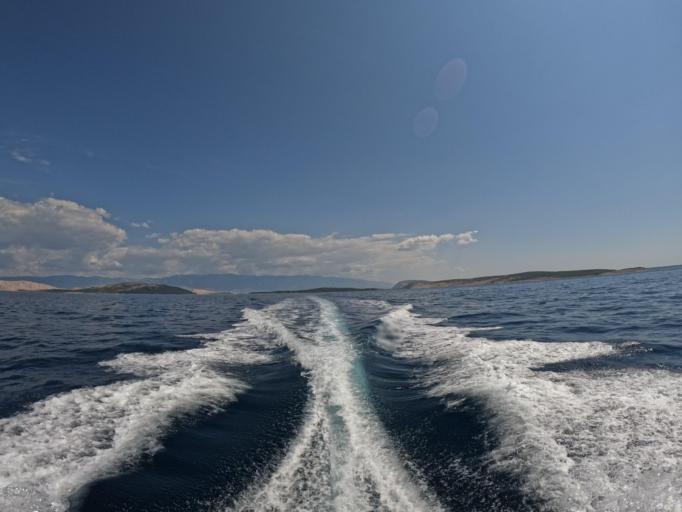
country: HR
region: Primorsko-Goranska
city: Lopar
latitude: 44.8669
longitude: 14.6812
